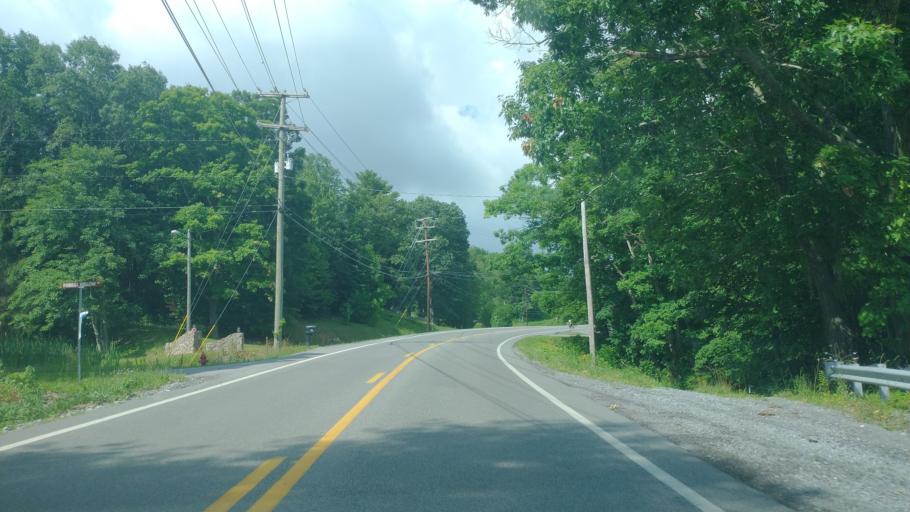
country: US
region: West Virginia
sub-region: Mercer County
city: Princeton
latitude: 37.3581
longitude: -81.1388
